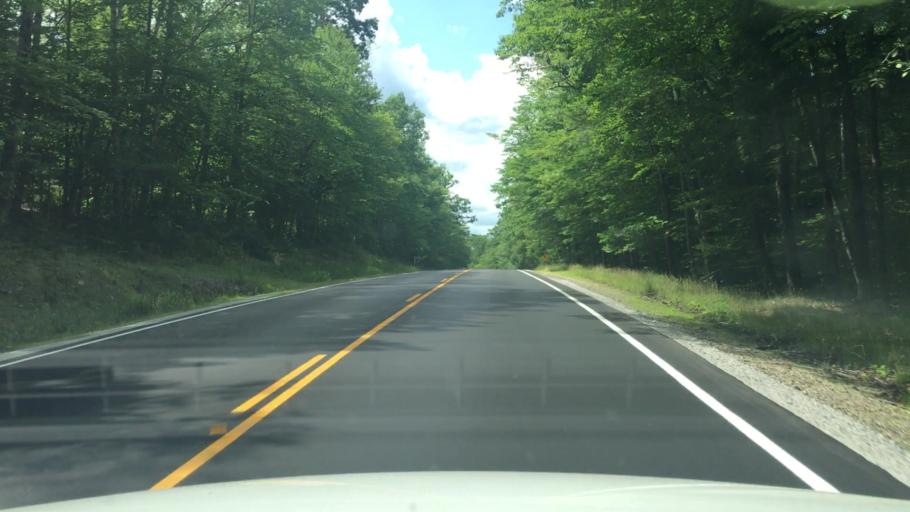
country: US
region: Maine
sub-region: Oxford County
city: West Paris
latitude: 44.3965
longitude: -70.6684
